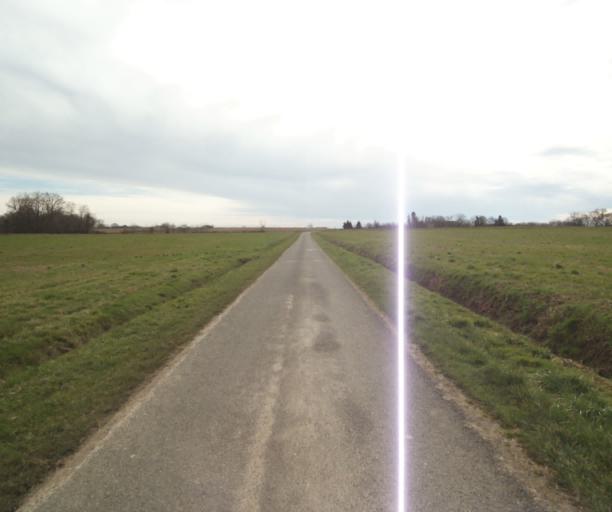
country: FR
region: Aquitaine
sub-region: Departement des Landes
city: Gabarret
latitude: 43.9246
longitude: 0.0444
